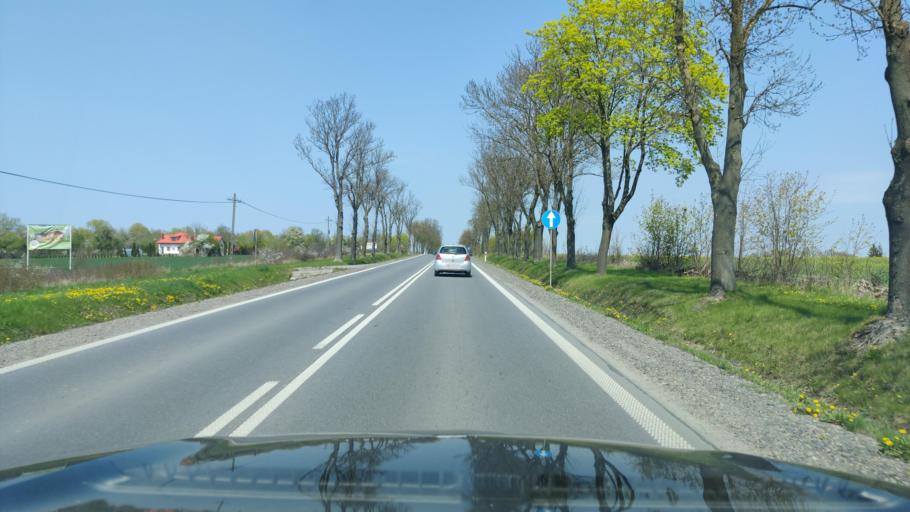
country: PL
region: Masovian Voivodeship
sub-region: Powiat pultuski
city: Pultusk
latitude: 52.6781
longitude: 21.0810
